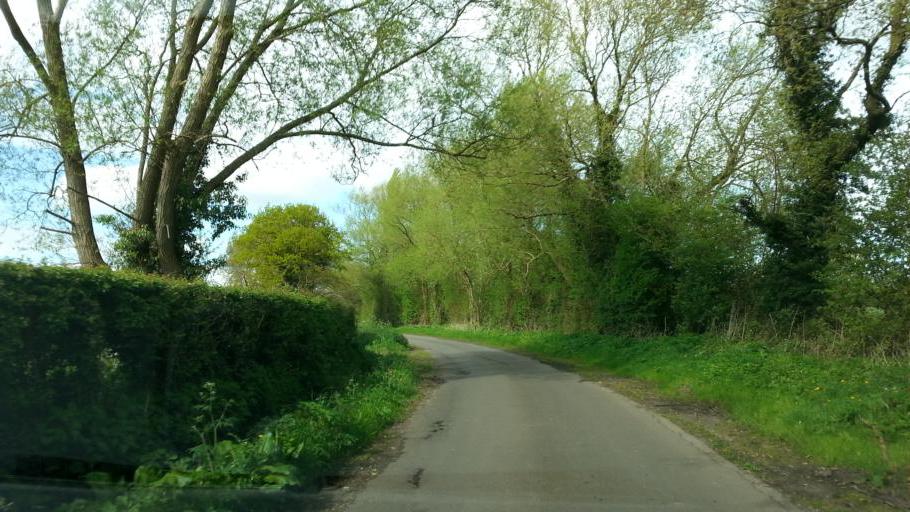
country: GB
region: England
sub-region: Derbyshire
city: Rodsley
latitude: 52.8879
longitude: -1.7443
